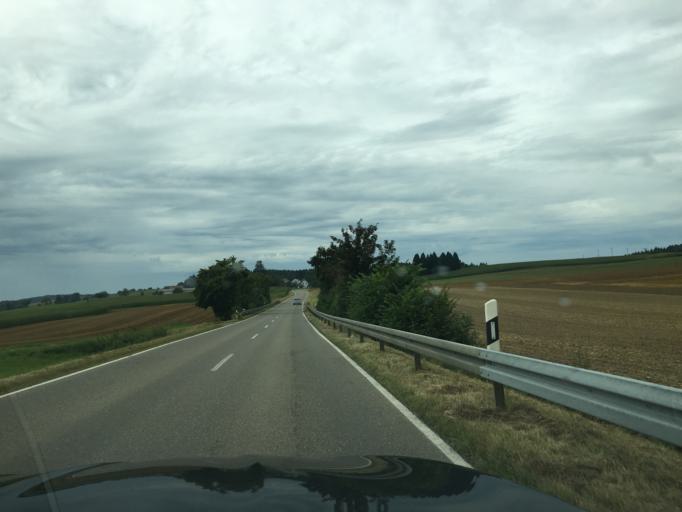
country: DE
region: Baden-Wuerttemberg
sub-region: Tuebingen Region
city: Wald
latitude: 47.9006
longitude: 9.1642
